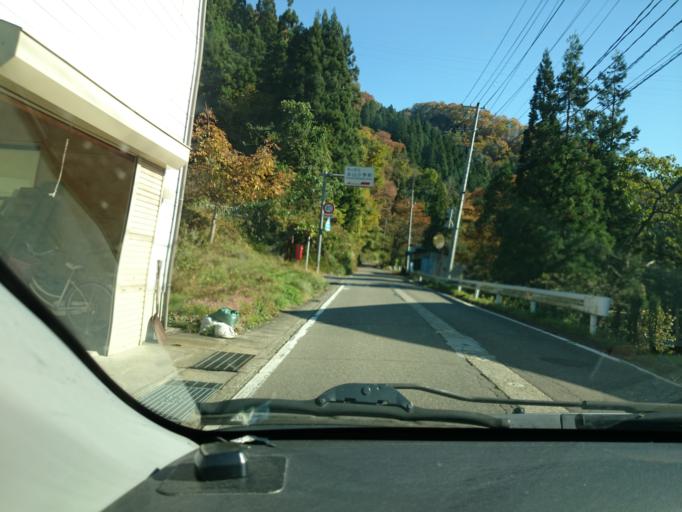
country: JP
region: Fukushima
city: Kitakata
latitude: 37.4508
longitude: 139.5243
